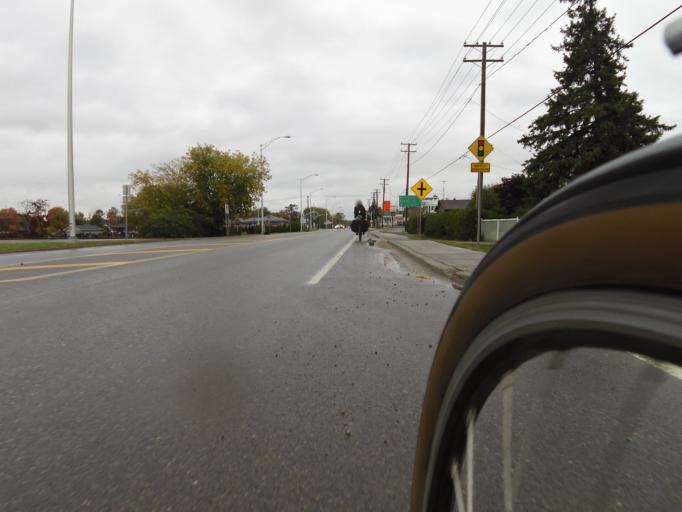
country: CA
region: Quebec
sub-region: Outaouais
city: Fort-Coulonge
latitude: 45.8492
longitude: -76.7256
